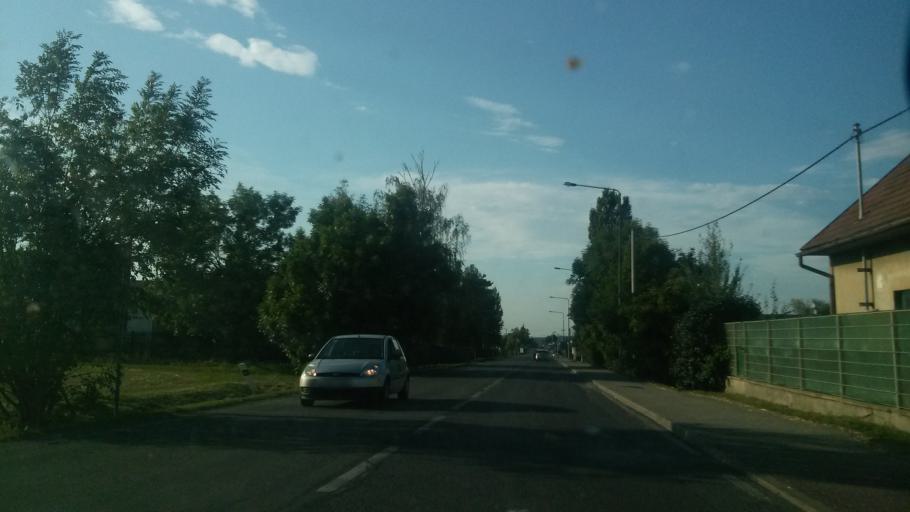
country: CZ
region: Central Bohemia
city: Vestec
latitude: 49.9803
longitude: 14.4978
